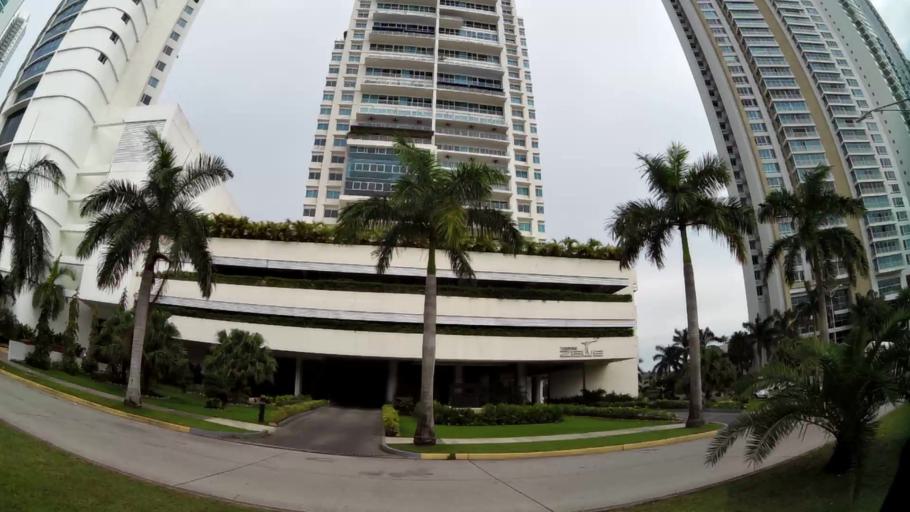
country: PA
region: Panama
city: San Miguelito
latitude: 9.0100
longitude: -79.4655
